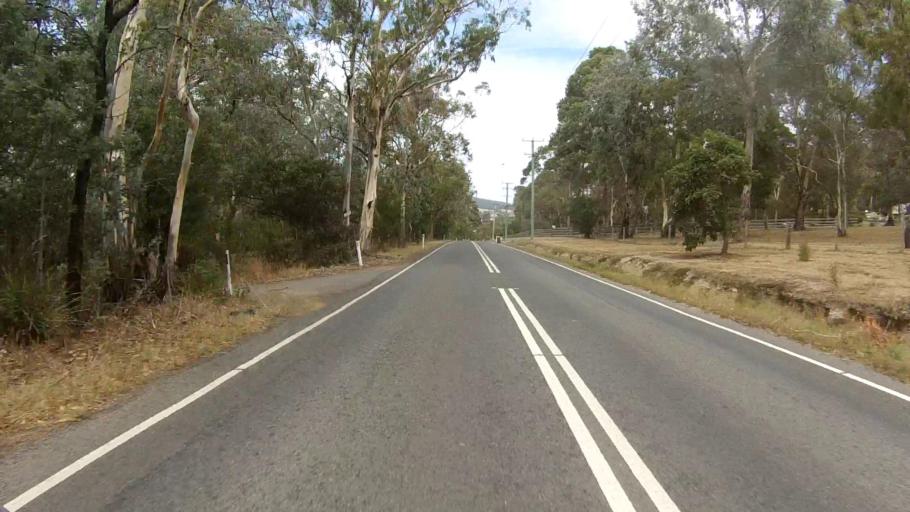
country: AU
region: Tasmania
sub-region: Clarence
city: Lauderdale
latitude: -42.8982
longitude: 147.4804
